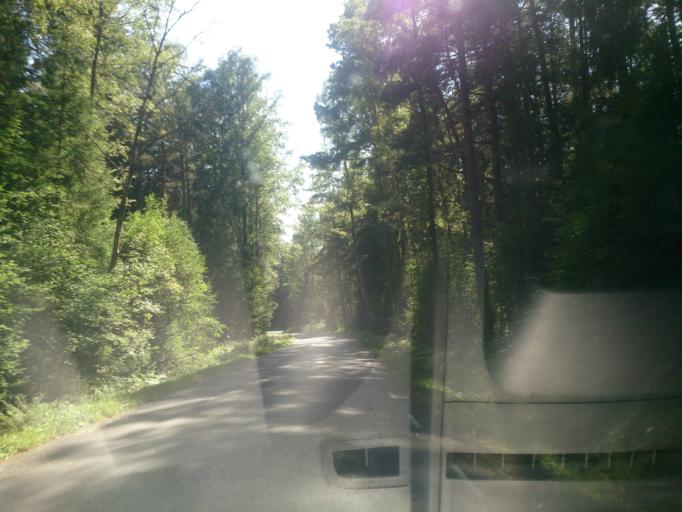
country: SE
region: OEstergoetland
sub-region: Norrkopings Kommun
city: Krokek
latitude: 58.5280
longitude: 16.6083
